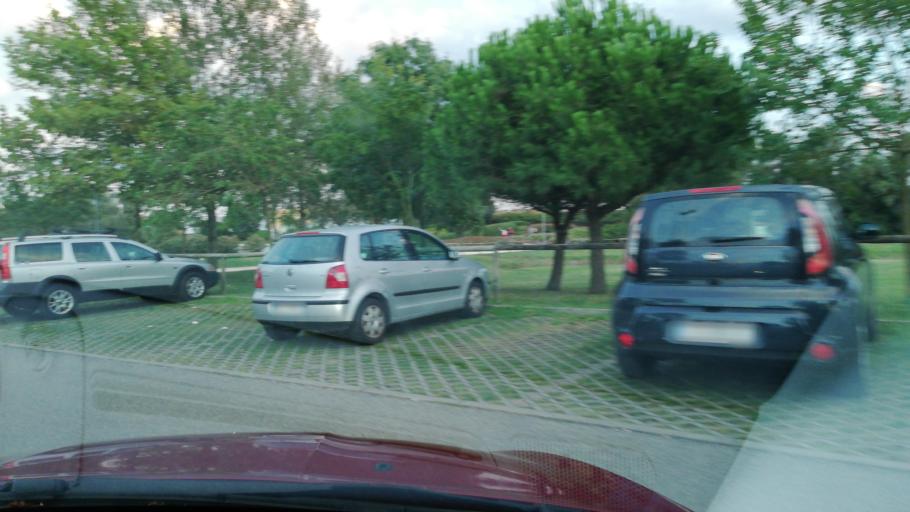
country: IT
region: Veneto
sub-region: Provincia di Venezia
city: Caorle
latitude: 45.5785
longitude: 12.8348
